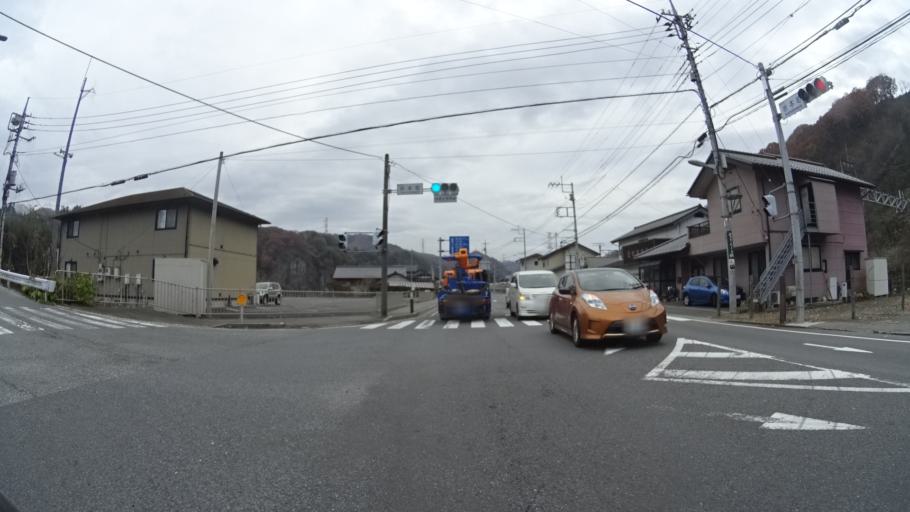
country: JP
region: Gunma
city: Numata
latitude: 36.6045
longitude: 139.0463
